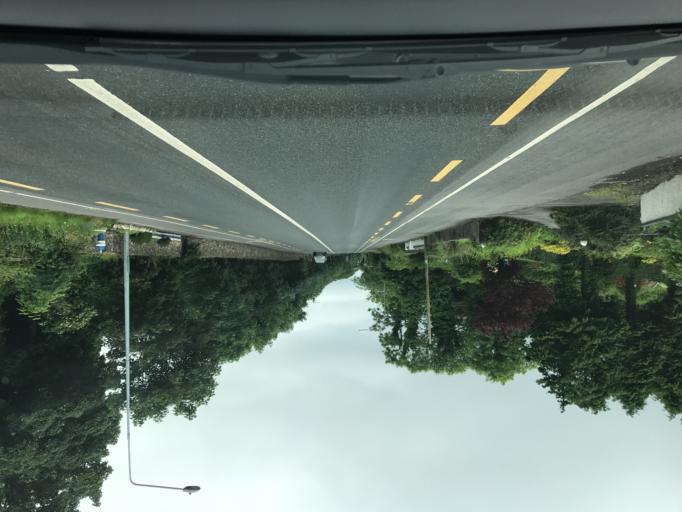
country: IE
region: Connaught
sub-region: Sligo
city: Strandhill
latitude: 54.3051
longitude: -8.5411
